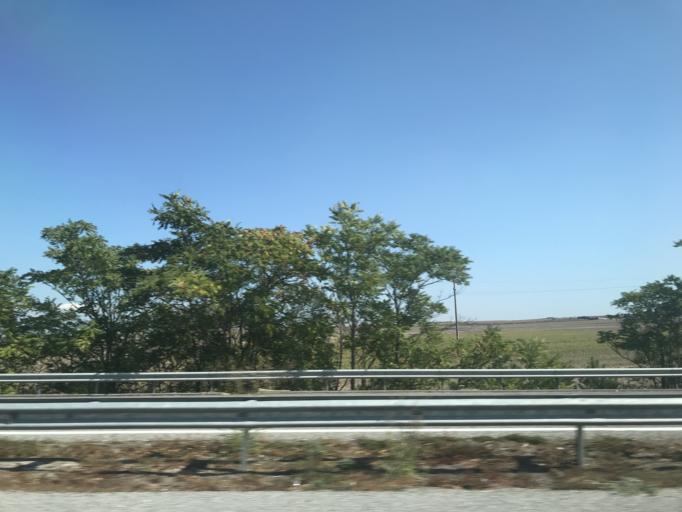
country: TR
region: Kirklareli
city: Luleburgaz
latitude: 41.4227
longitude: 27.3847
